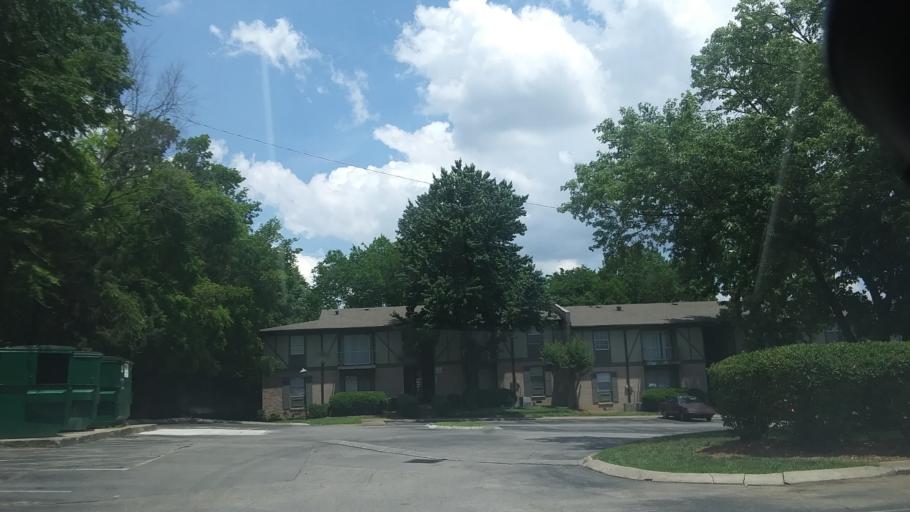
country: US
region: Tennessee
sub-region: Davidson County
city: Oak Hill
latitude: 36.0799
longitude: -86.7005
